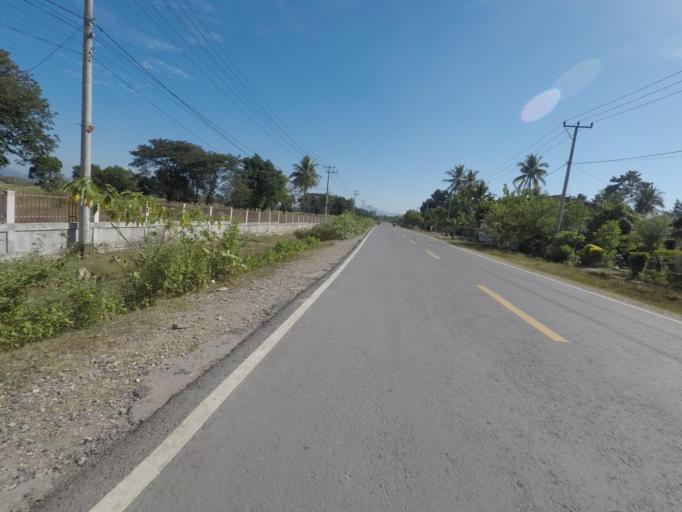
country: TL
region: Bobonaro
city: Maliana
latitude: -8.9772
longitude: 125.2201
